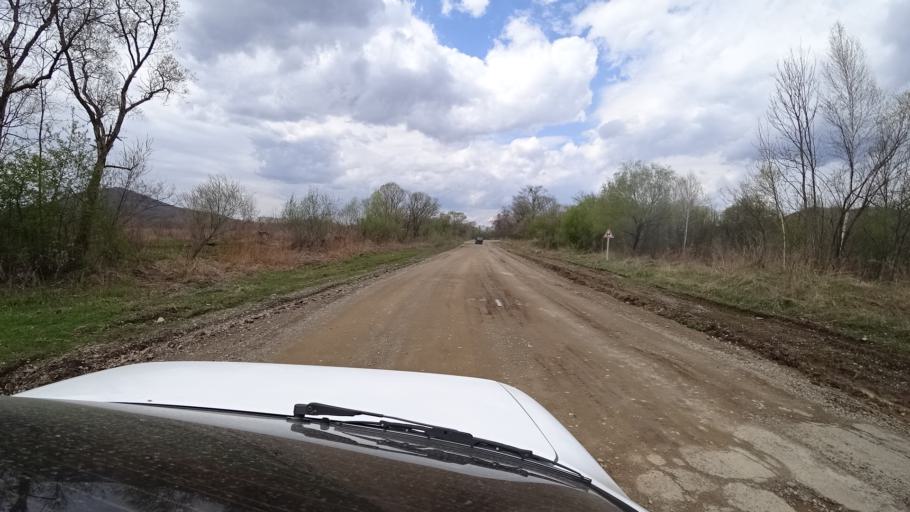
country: RU
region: Primorskiy
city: Novopokrovka
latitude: 45.6099
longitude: 134.2758
